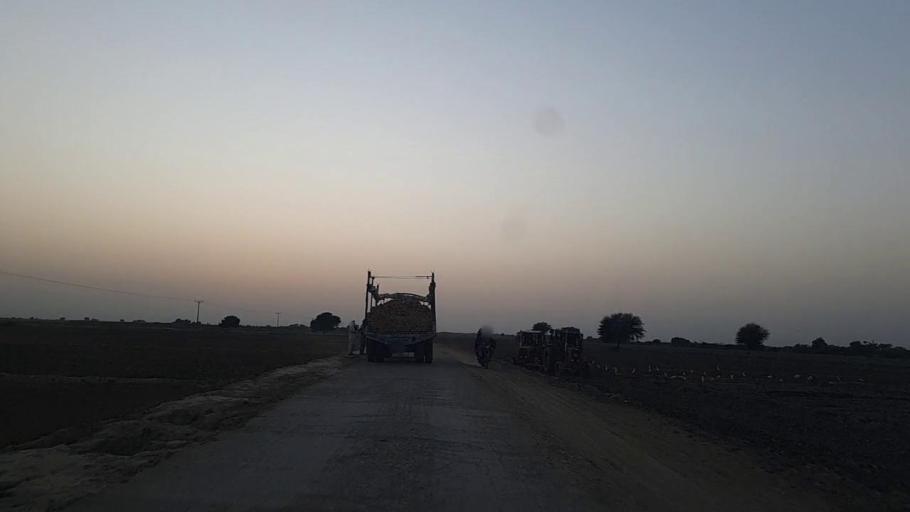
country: PK
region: Sindh
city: Naukot
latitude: 24.7528
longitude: 69.2978
